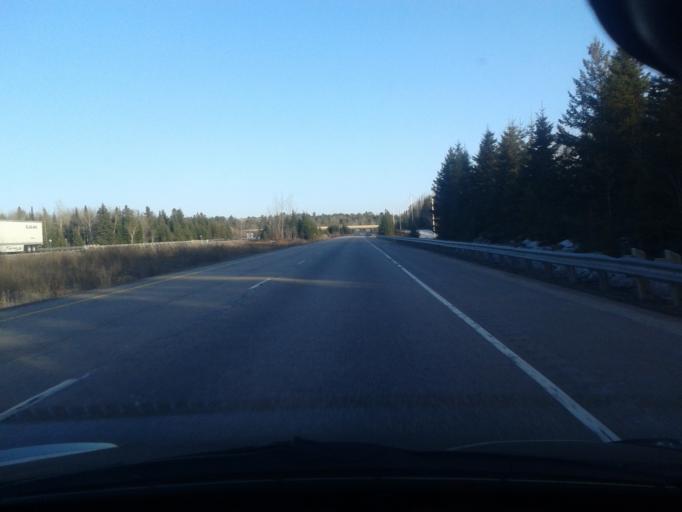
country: CA
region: Ontario
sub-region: Nipissing District
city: North Bay
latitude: 46.2413
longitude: -79.3572
